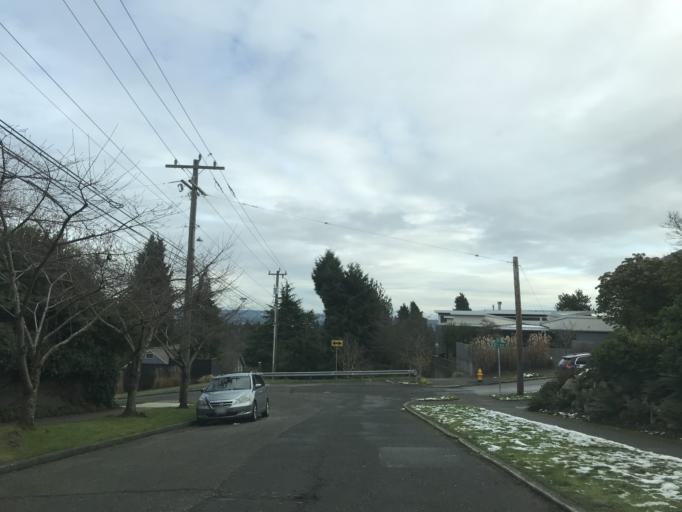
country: US
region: Washington
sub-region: King County
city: Seattle
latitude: 47.6323
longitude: -122.3040
